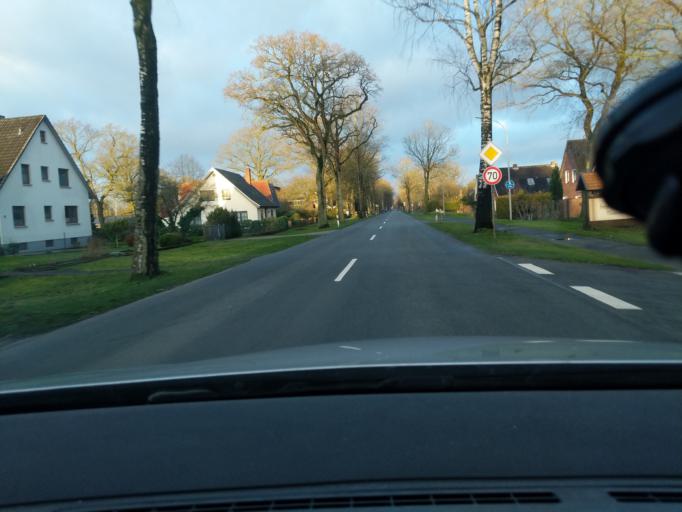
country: DE
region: Lower Saxony
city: Drangstedt
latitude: 53.6741
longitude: 8.7050
